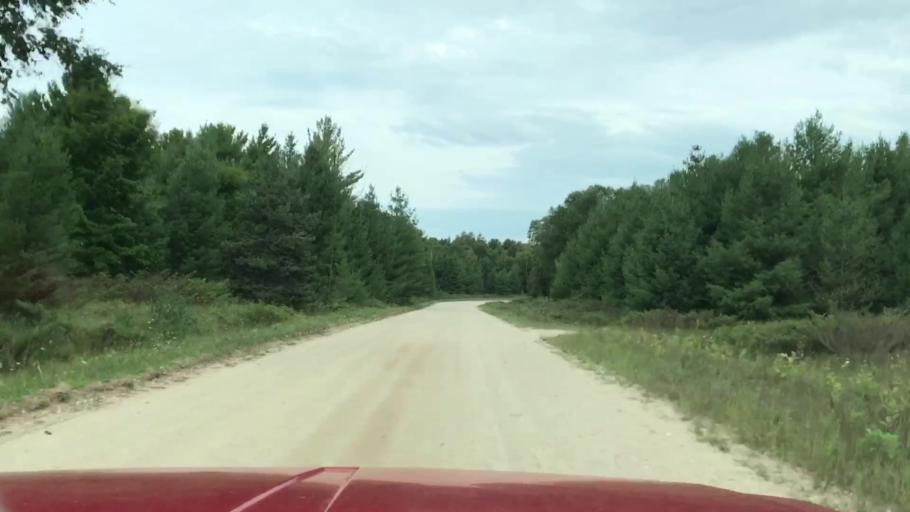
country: US
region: Michigan
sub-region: Charlevoix County
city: Charlevoix
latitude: 45.7207
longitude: -85.5590
